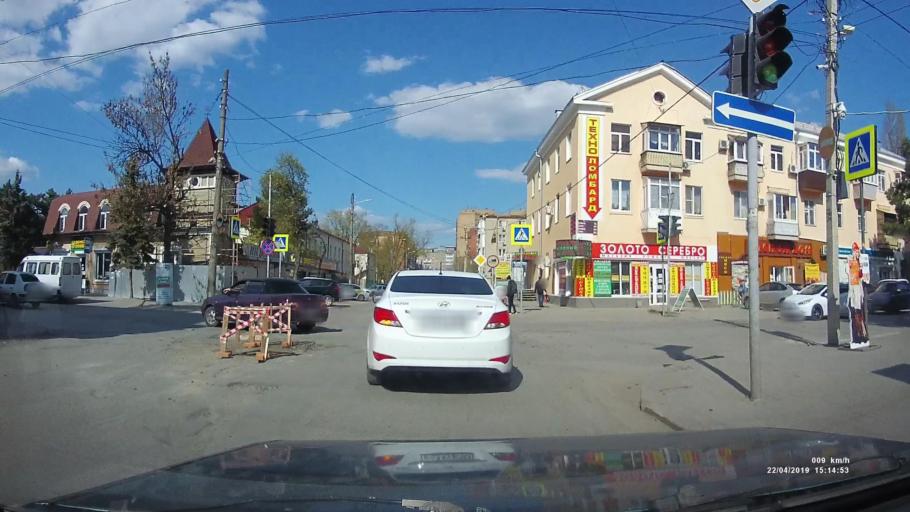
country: RU
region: Rostov
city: Azov
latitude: 47.1051
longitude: 39.4269
